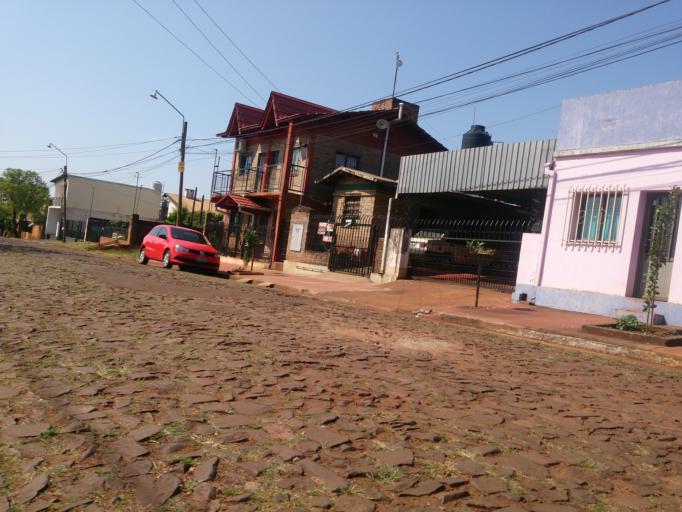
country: AR
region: Misiones
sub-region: Departamento de Obera
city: Obera
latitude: -27.4869
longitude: -55.1079
